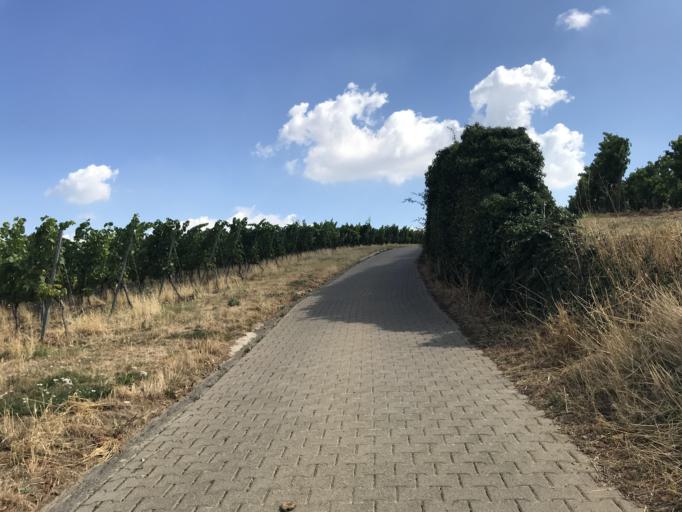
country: DE
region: Rheinland-Pfalz
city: Schwabenheim
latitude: 49.9451
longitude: 8.0889
